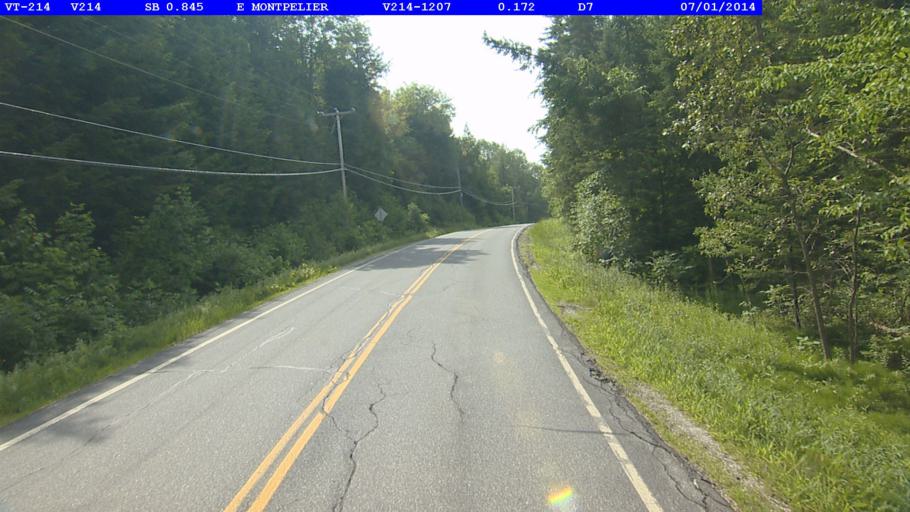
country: US
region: Vermont
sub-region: Washington County
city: Barre
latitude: 44.2883
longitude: -72.4422
